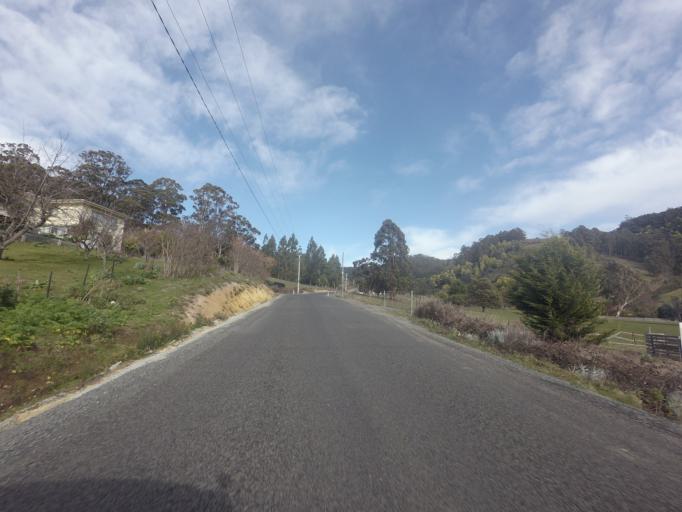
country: AU
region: Tasmania
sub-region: Kingborough
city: Margate
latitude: -42.9931
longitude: 147.1850
